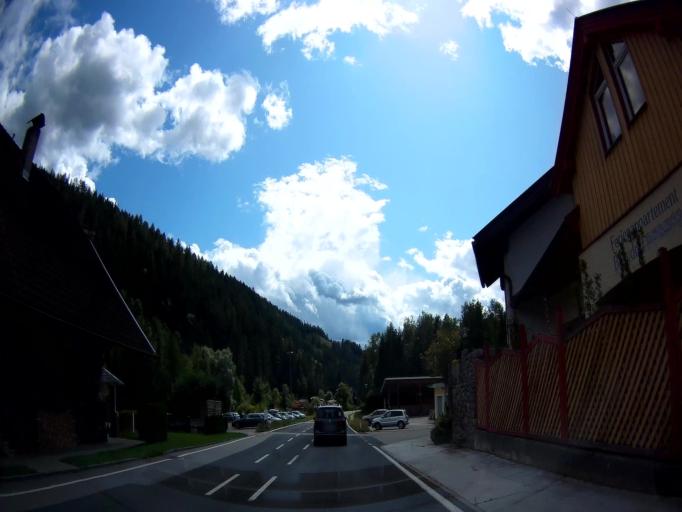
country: AT
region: Carinthia
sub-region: Politischer Bezirk Spittal an der Drau
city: Trebesing
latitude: 46.8821
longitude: 13.5137
